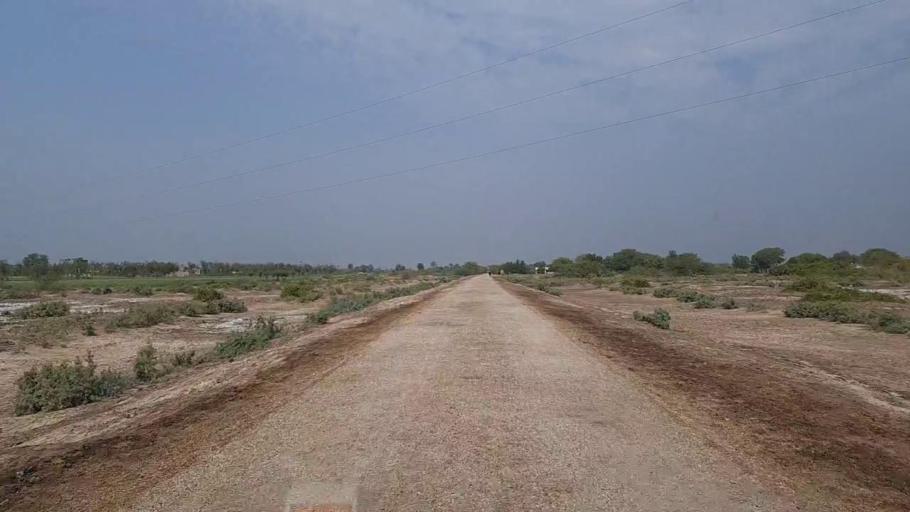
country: PK
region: Sindh
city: Mirwah Gorchani
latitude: 25.3389
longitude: 69.0410
